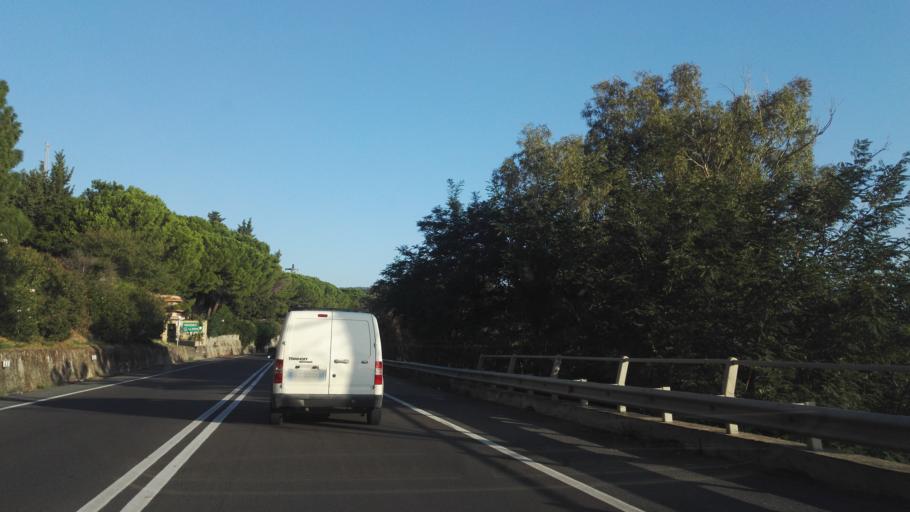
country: IT
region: Calabria
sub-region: Provincia di Catanzaro
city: Squillace Lido
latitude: 38.7668
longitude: 16.5629
